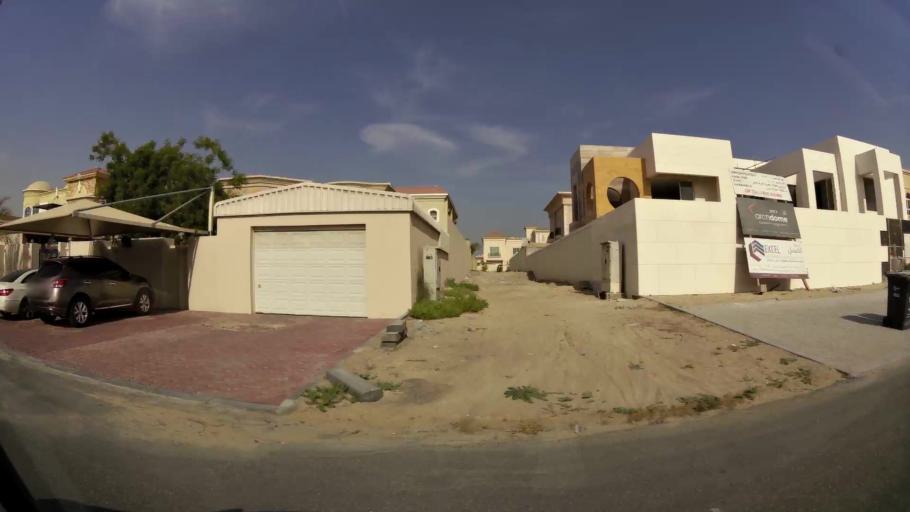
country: AE
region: Ash Shariqah
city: Sharjah
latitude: 25.2421
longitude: 55.4142
